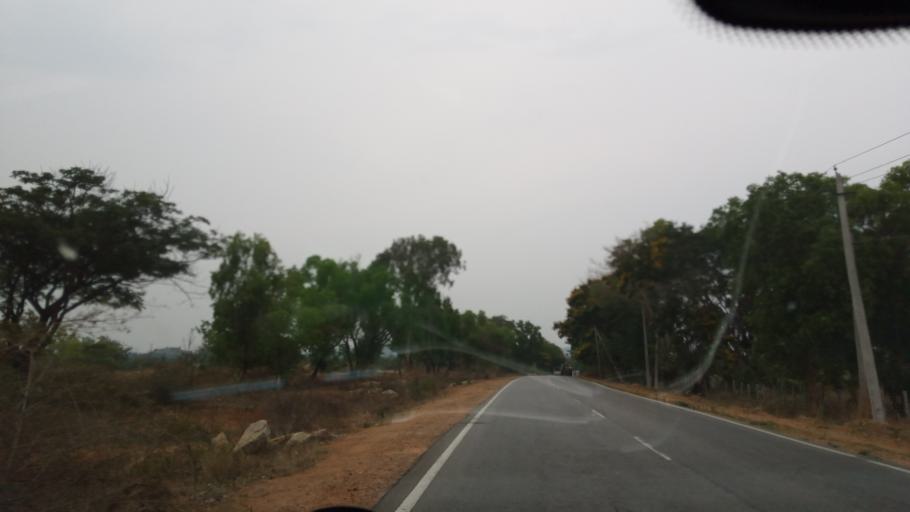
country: IN
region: Karnataka
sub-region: Mandya
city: Belluru
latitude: 12.9528
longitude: 76.7540
